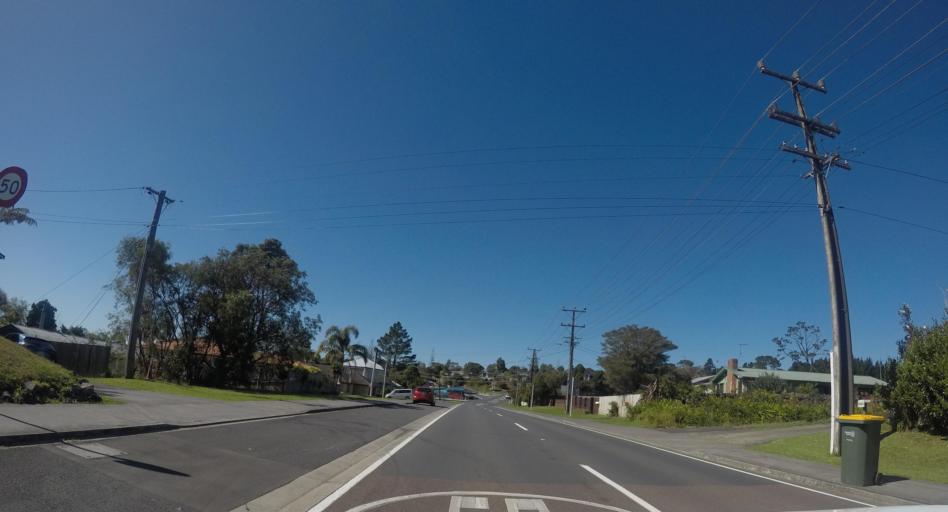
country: NZ
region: Auckland
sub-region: Auckland
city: Waitakere
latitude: -36.8976
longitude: 174.6116
